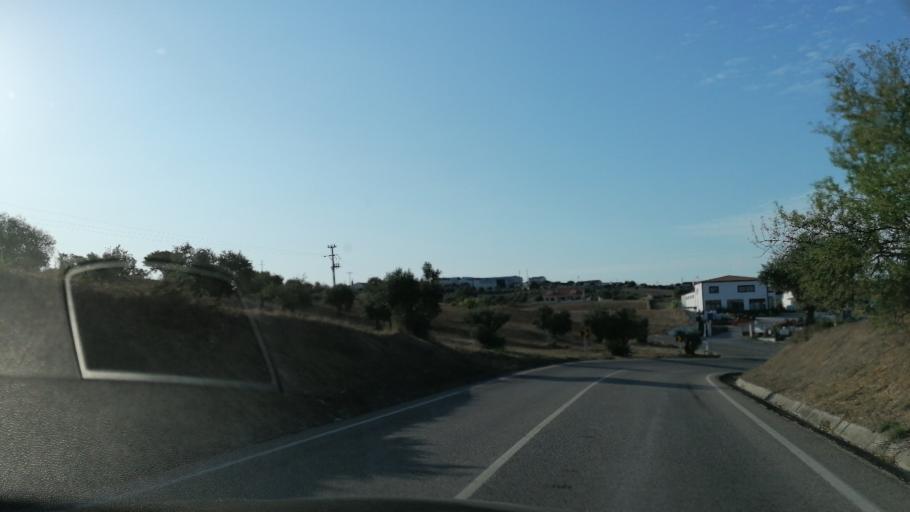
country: PT
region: Santarem
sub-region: Alcanena
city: Alcanena
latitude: 39.3535
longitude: -8.6643
